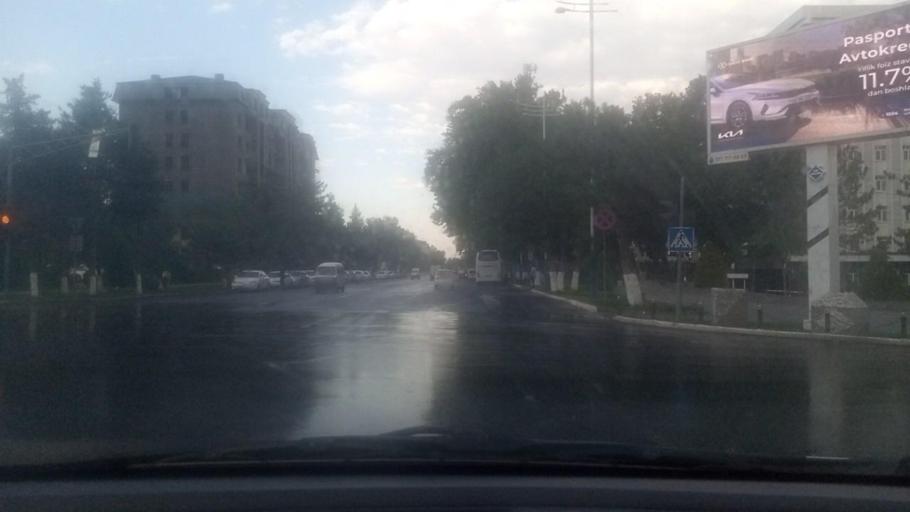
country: UZ
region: Toshkent Shahri
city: Tashkent
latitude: 41.2955
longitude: 69.1765
